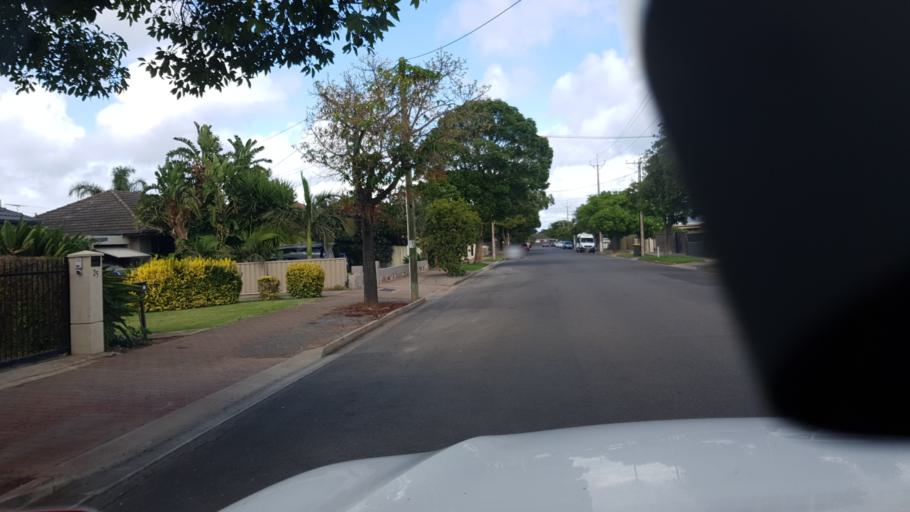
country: AU
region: South Australia
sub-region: Adelaide
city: Brighton
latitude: -35.0242
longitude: 138.5271
